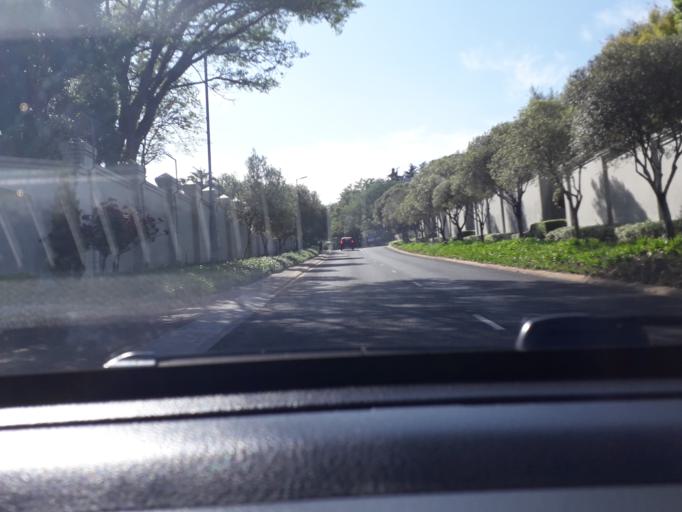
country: ZA
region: Gauteng
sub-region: City of Johannesburg Metropolitan Municipality
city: Midrand
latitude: -26.0456
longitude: 28.0304
